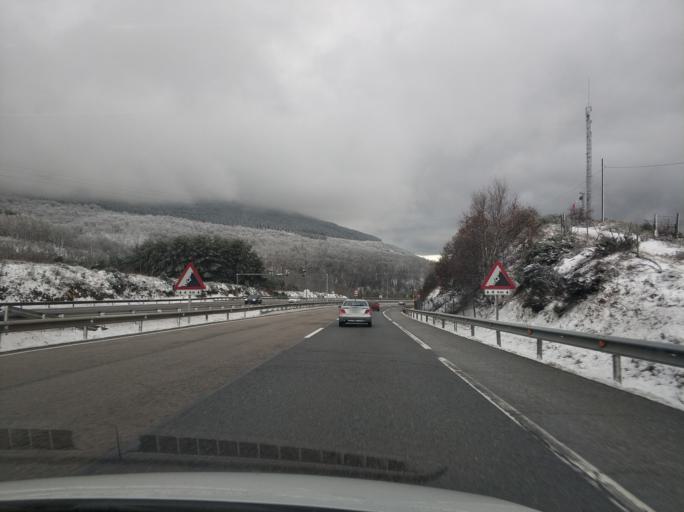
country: ES
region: Madrid
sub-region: Provincia de Madrid
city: Somosierra
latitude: 41.1277
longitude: -3.5804
